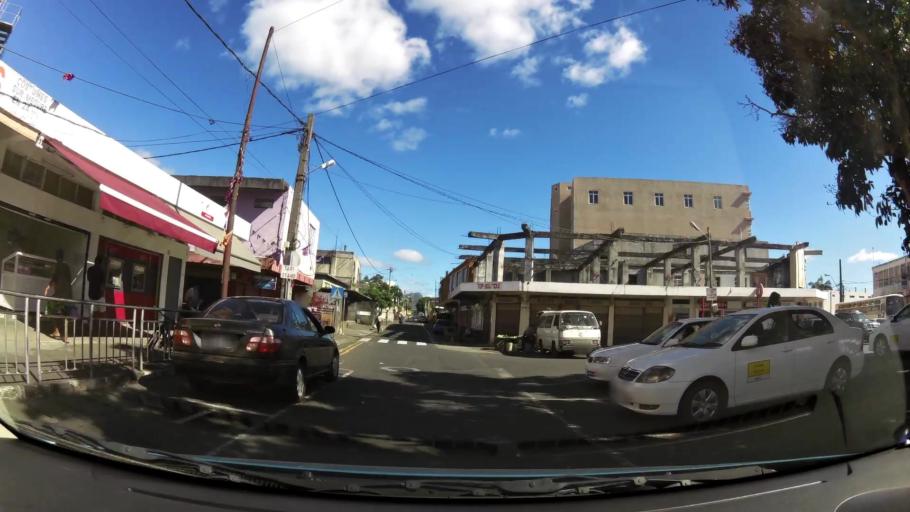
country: MU
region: Plaines Wilhems
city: Quatre Bornes
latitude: -20.2713
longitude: 57.4747
